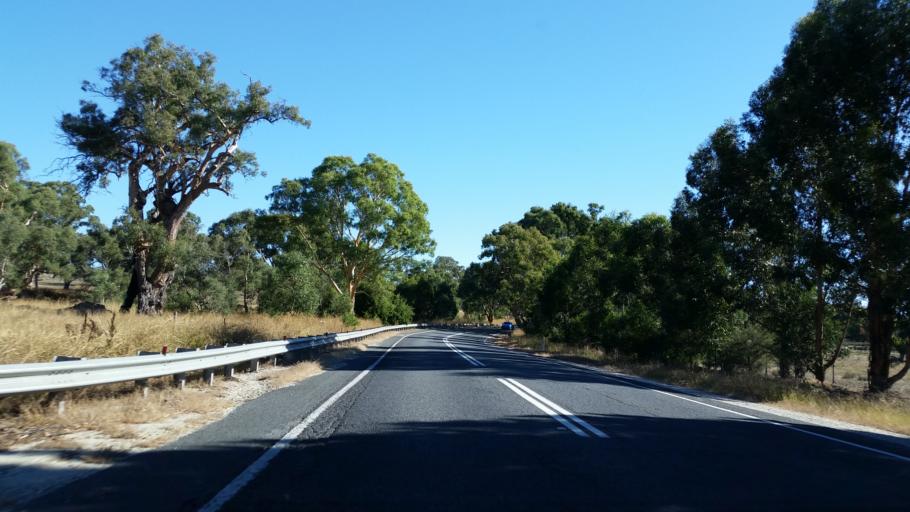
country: AU
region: South Australia
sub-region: Adelaide Hills
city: Birdwood
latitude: -34.8032
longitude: 138.9924
